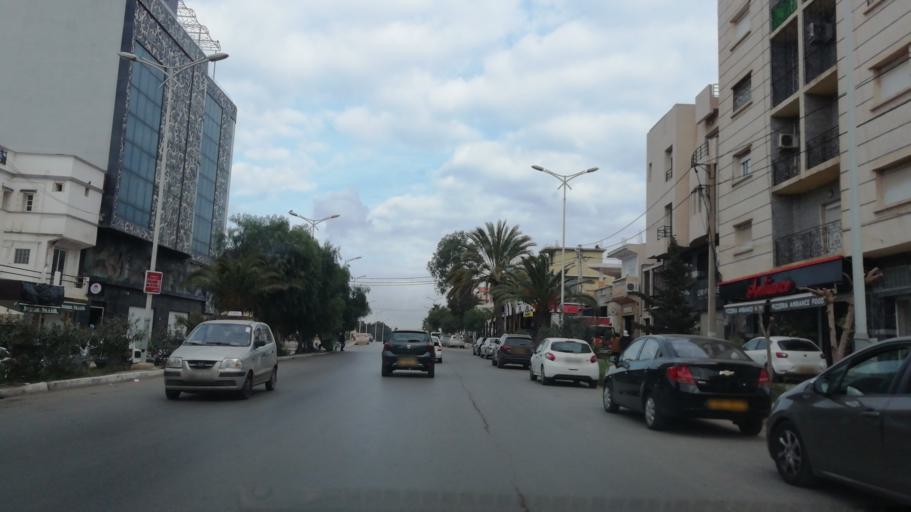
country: DZ
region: Oran
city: Oran
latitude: 35.7112
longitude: -0.6116
